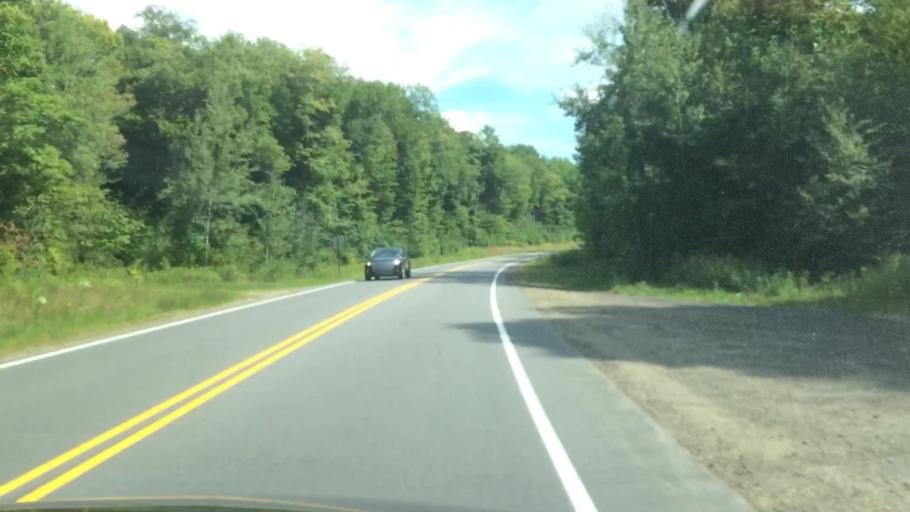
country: US
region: Pennsylvania
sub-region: McKean County
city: Bradford
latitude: 41.8837
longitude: -78.5803
